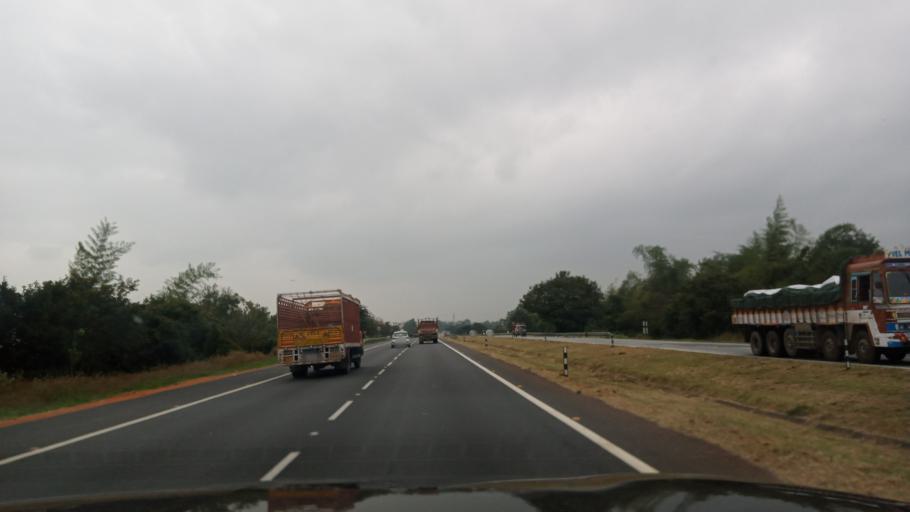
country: IN
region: Karnataka
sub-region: Bangalore Rural
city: Nelamangala
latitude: 13.0057
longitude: 77.4745
